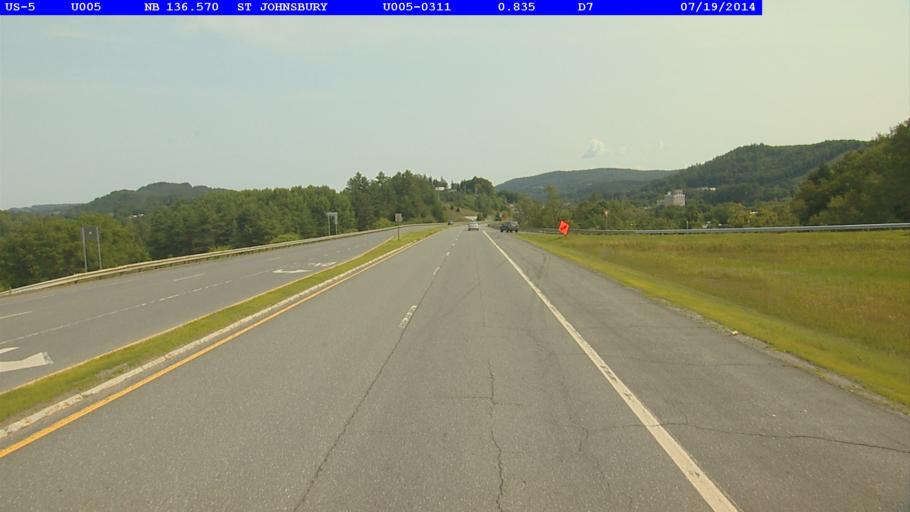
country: US
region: Vermont
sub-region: Caledonia County
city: Saint Johnsbury
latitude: 44.4061
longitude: -72.0221
